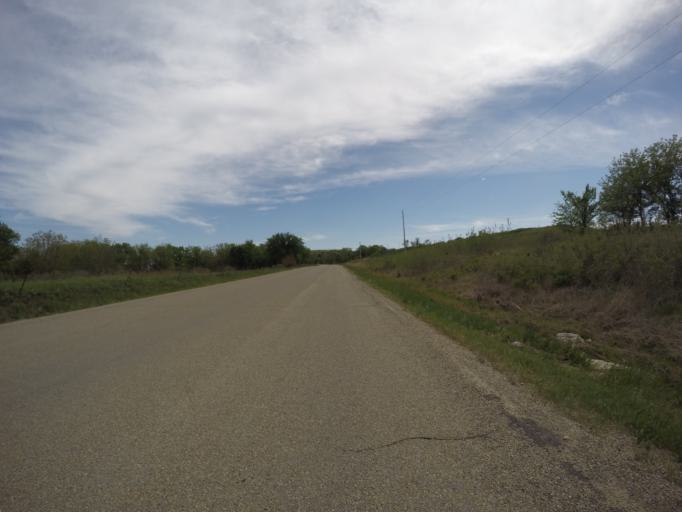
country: US
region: Kansas
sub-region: Riley County
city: Ogden
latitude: 39.0610
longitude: -96.6514
